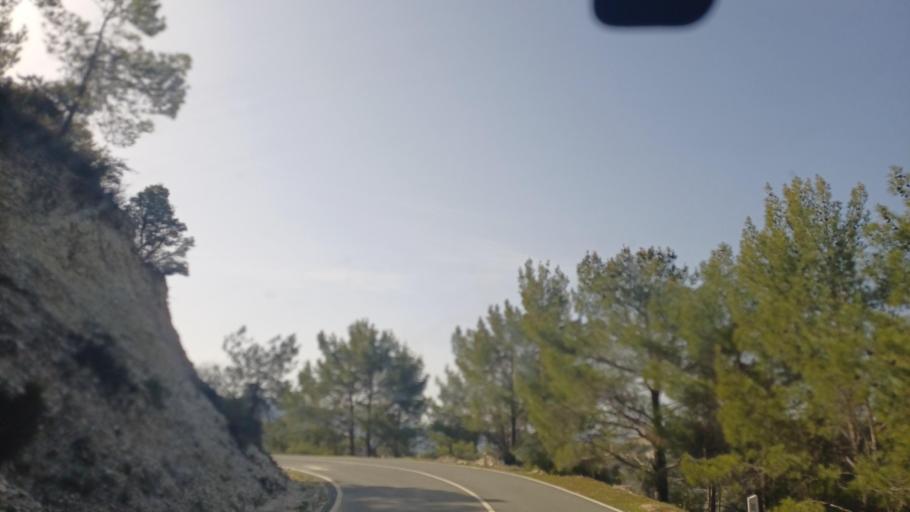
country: CY
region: Limassol
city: Pachna
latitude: 34.8814
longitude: 32.7293
